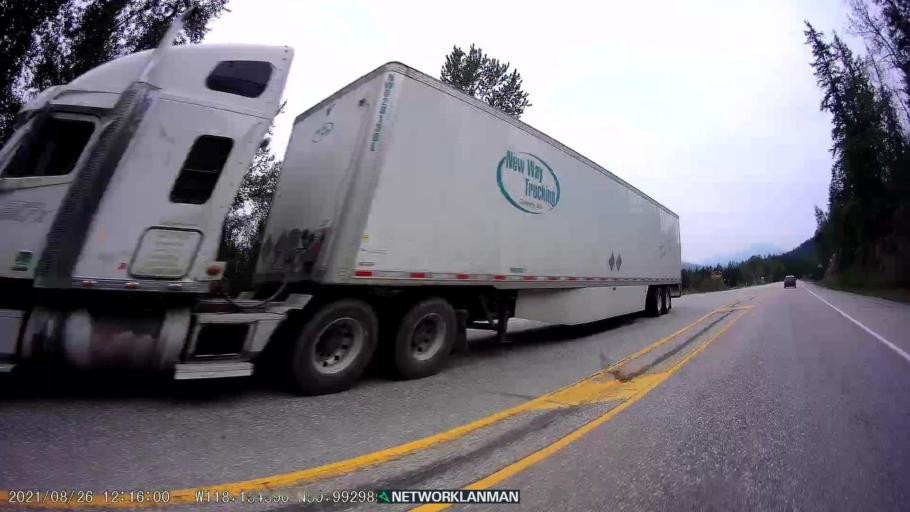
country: CA
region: British Columbia
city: Revelstoke
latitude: 50.9931
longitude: -118.1551
